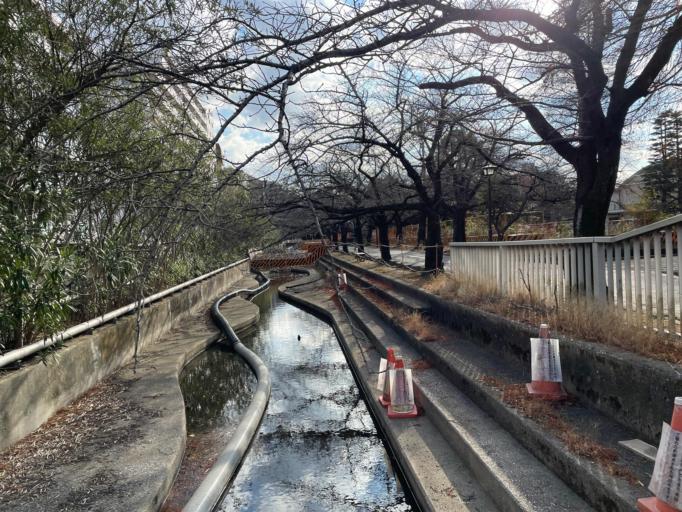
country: JP
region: Tokyo
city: Urayasu
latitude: 35.6822
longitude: 139.8391
